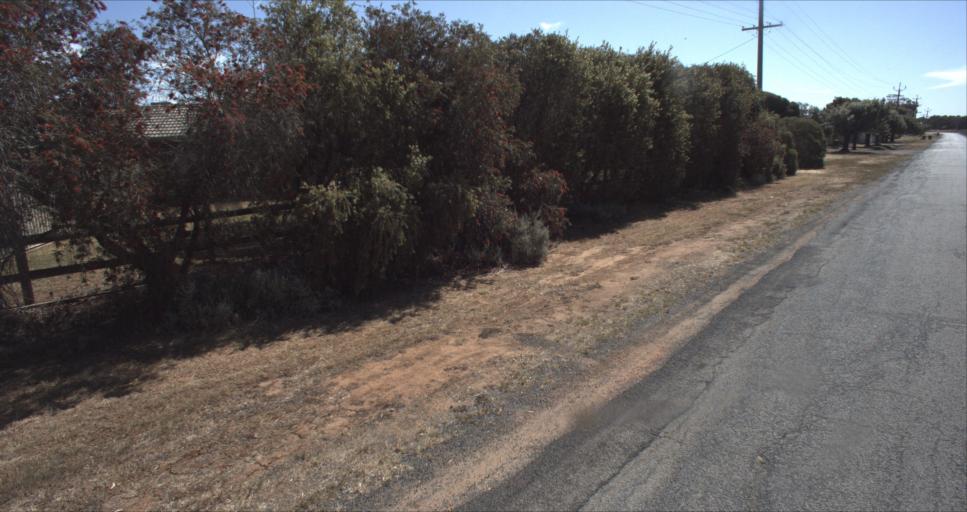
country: AU
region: New South Wales
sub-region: Leeton
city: Leeton
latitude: -34.5506
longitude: 146.3826
